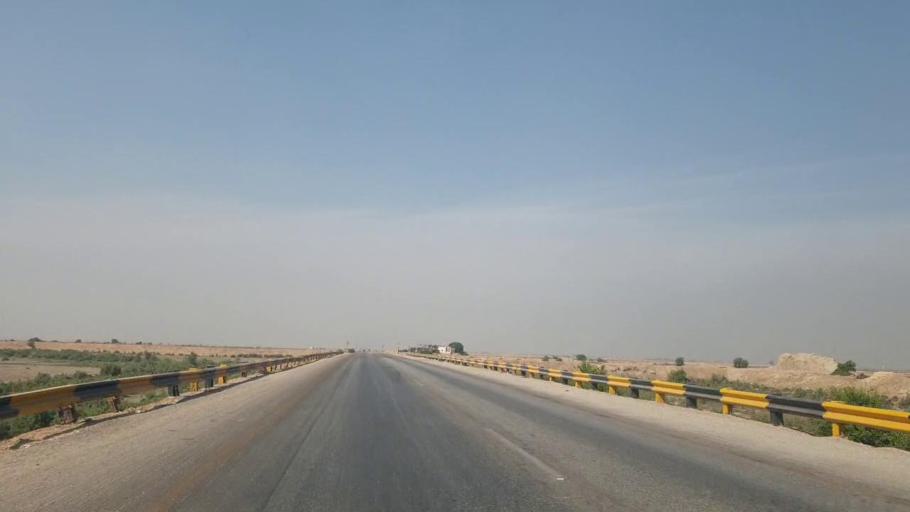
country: PK
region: Sindh
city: Hala
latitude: 25.8791
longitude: 68.2489
